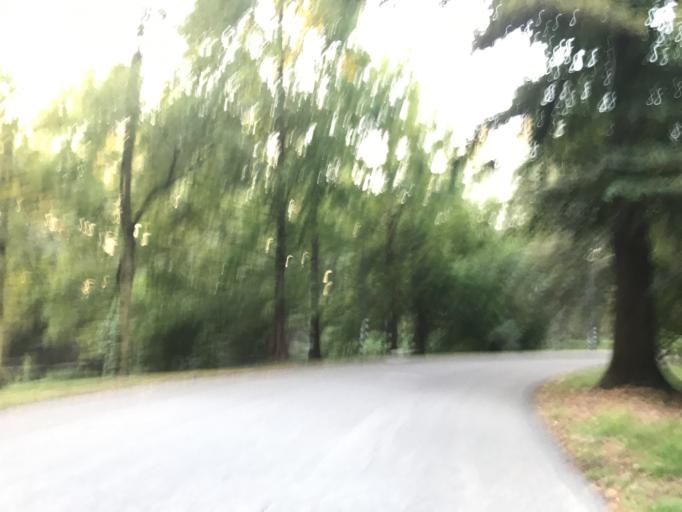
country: IT
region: Lombardy
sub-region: Citta metropolitana di Milano
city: Sesto San Giovanni
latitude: 45.4959
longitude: 9.2484
